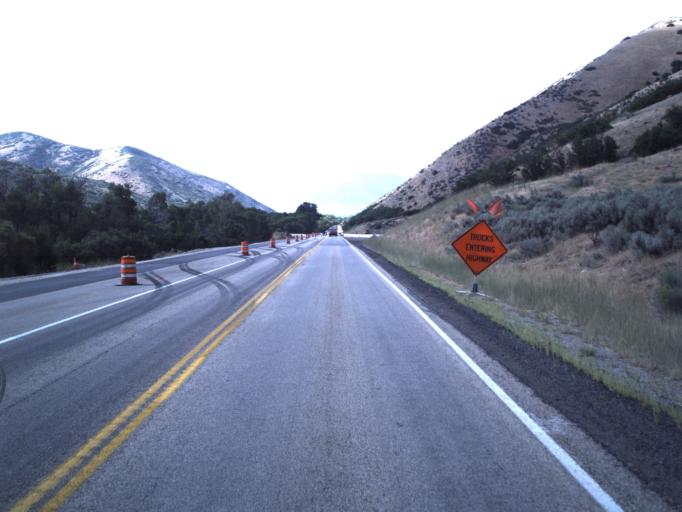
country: US
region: Utah
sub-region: Wasatch County
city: Heber
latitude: 40.4237
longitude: -111.3446
